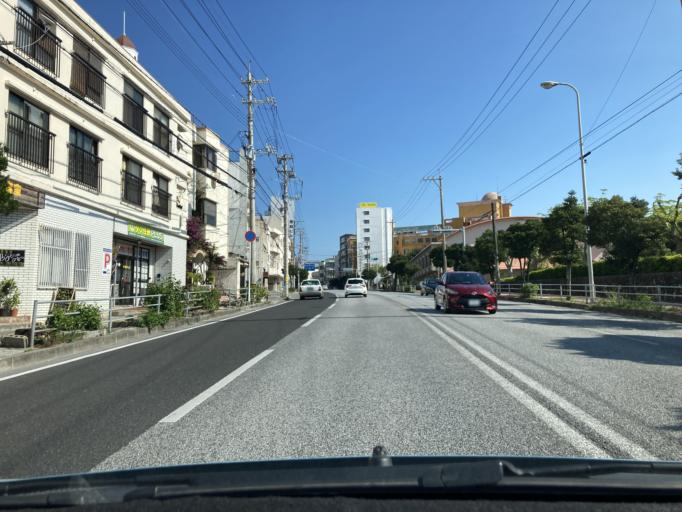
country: JP
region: Okinawa
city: Naha-shi
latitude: 26.2065
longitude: 127.6949
